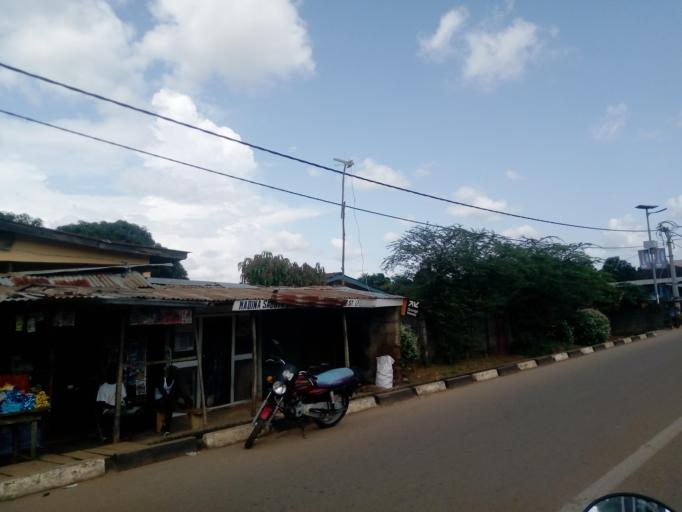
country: SL
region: Northern Province
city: Makeni
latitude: 8.8972
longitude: -12.0412
